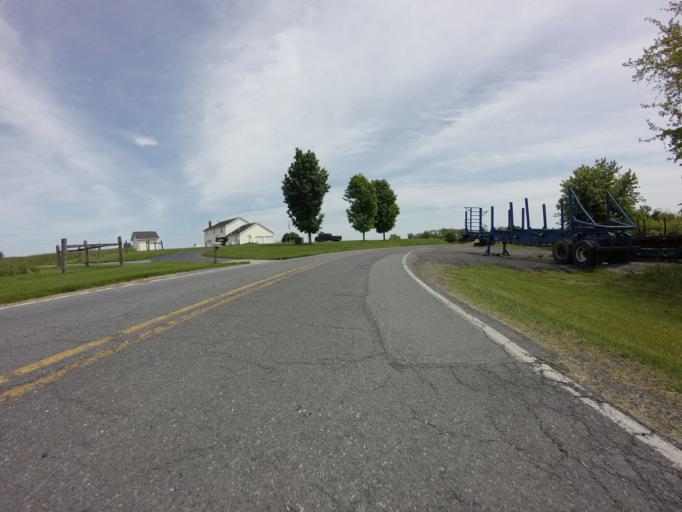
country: US
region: Maryland
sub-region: Frederick County
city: Linganore
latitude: 39.5037
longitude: -77.2036
